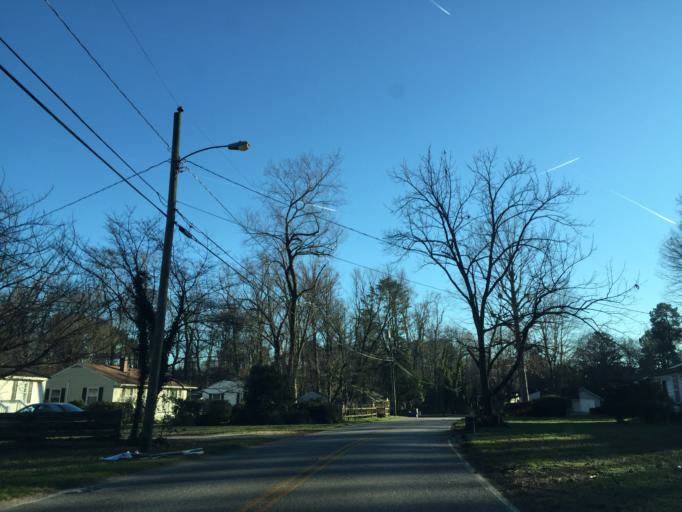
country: US
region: Virginia
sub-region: City of Newport News
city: Newport News
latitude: 37.0811
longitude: -76.5141
